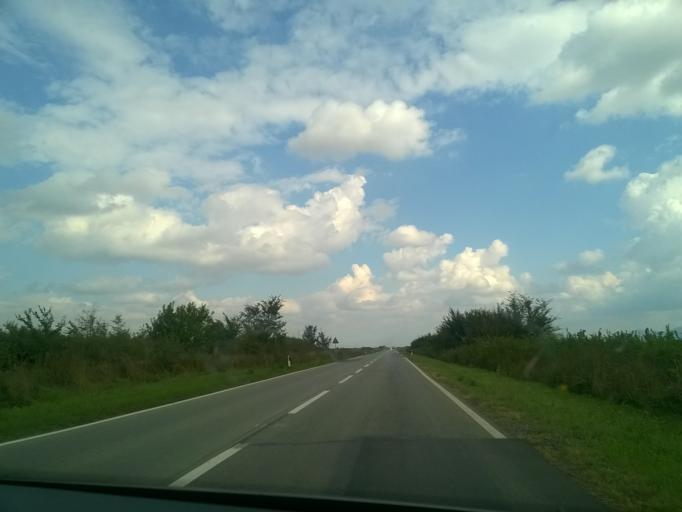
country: RS
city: Margita
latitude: 45.2249
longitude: 21.1561
